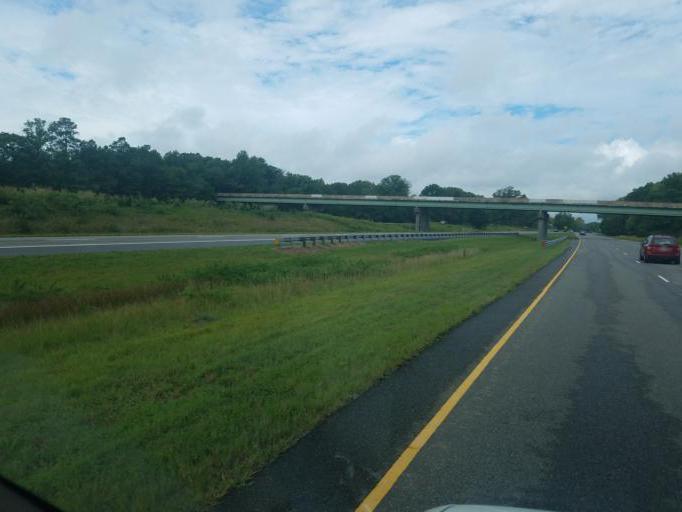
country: US
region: Virginia
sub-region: Henrico County
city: Sandston
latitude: 37.5236
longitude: -77.2791
